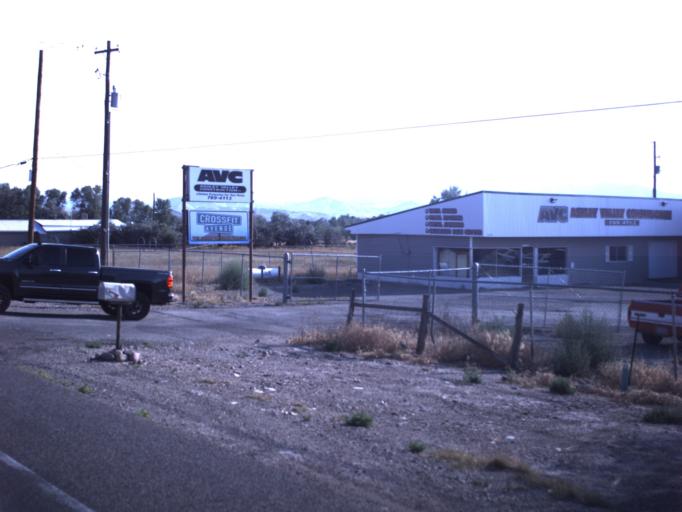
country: US
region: Utah
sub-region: Uintah County
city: Vernal
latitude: 40.4793
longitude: -109.5289
